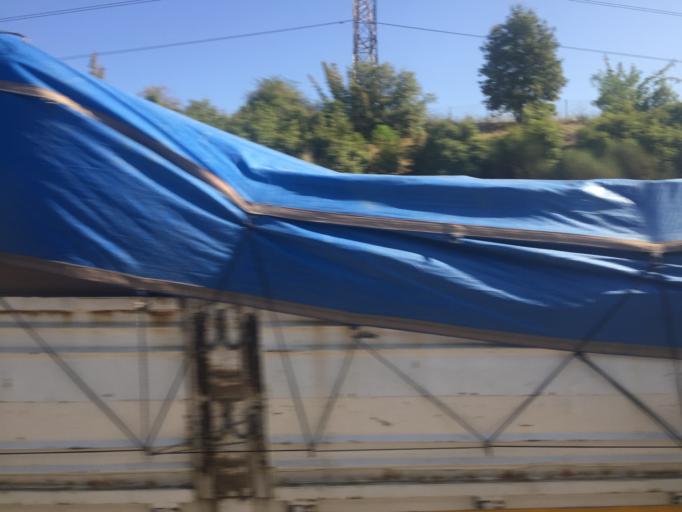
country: TR
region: Bursa
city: Demirtas
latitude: 40.2859
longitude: 29.0753
